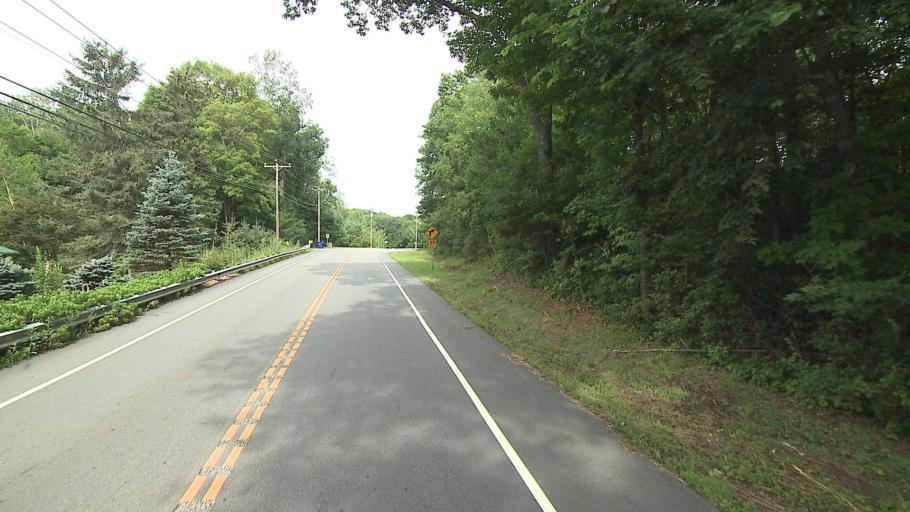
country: US
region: Connecticut
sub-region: Litchfield County
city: New Preston
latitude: 41.7087
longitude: -73.3031
